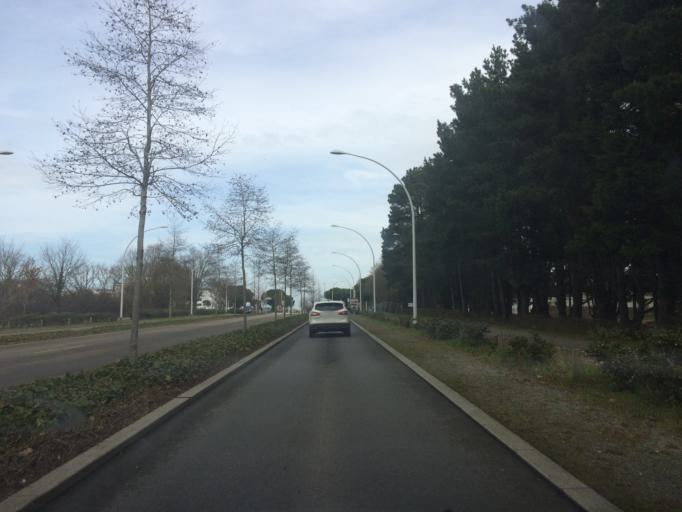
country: FR
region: Pays de la Loire
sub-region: Departement de la Loire-Atlantique
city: Saint-Nazaire
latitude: 47.2630
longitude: -2.2599
